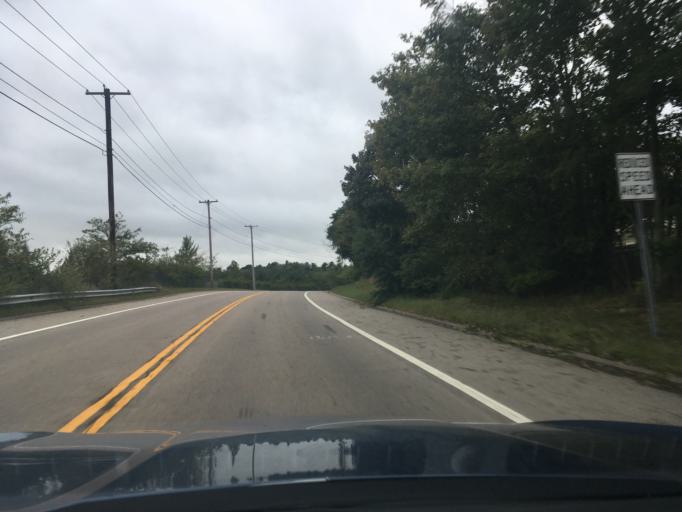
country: US
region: Rhode Island
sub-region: Kent County
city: East Greenwich
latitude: 41.6101
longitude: -71.4719
